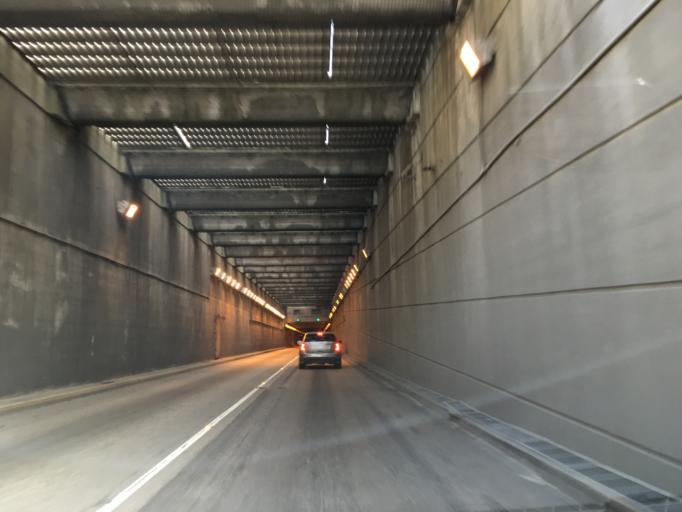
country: CA
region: British Columbia
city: Ladner
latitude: 49.1247
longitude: -123.0794
